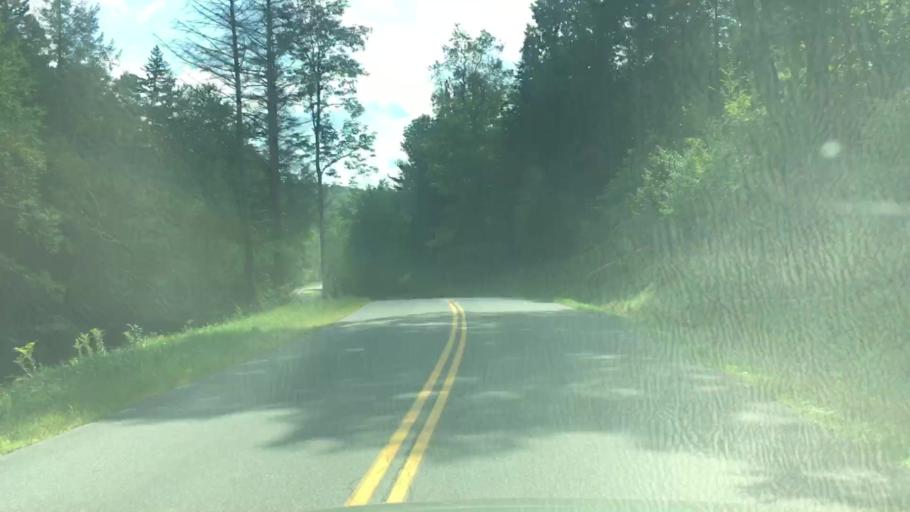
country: US
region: Vermont
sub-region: Windham County
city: Dover
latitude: 42.8162
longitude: -72.7516
